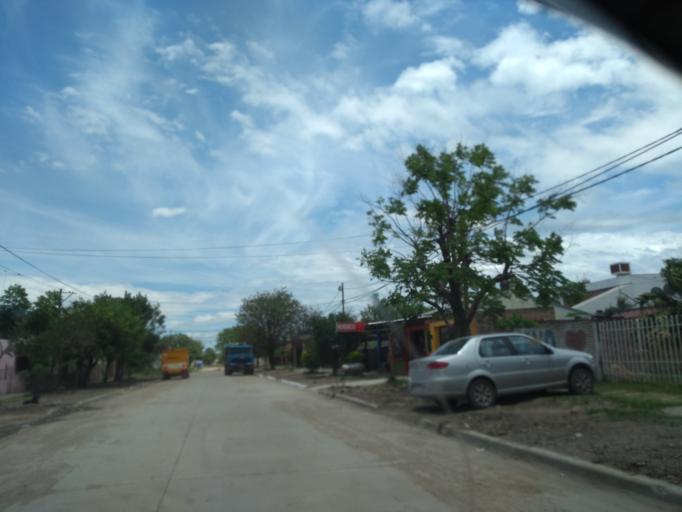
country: AR
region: Chaco
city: Resistencia
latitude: -27.4713
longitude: -58.9696
